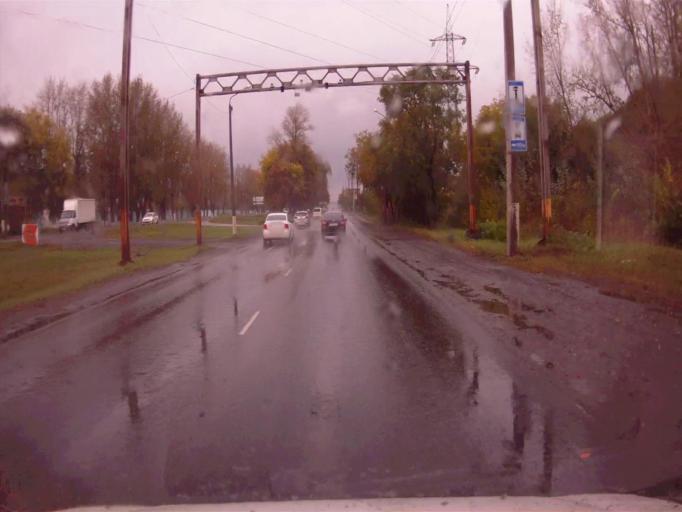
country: RU
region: Chelyabinsk
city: Dolgoderevenskoye
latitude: 55.2488
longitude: 61.3573
